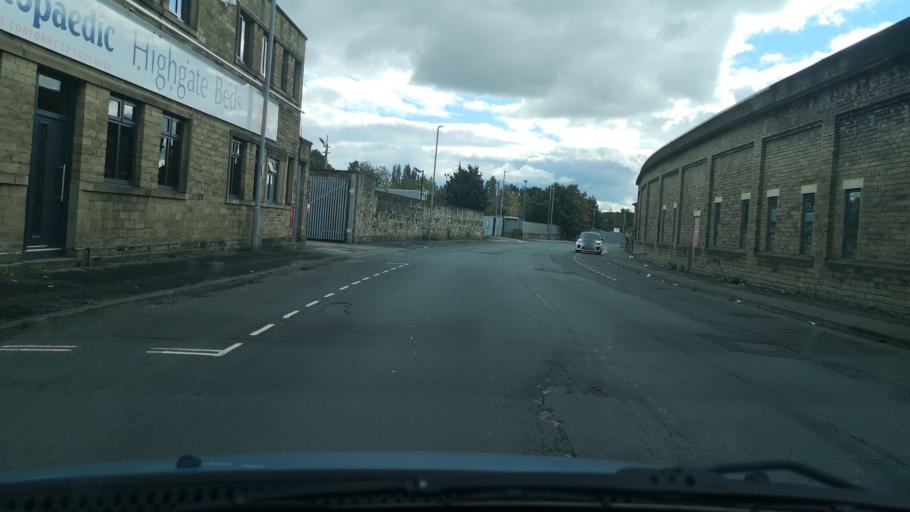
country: GB
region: England
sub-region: Kirklees
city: Dewsbury
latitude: 53.6853
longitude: -1.6235
